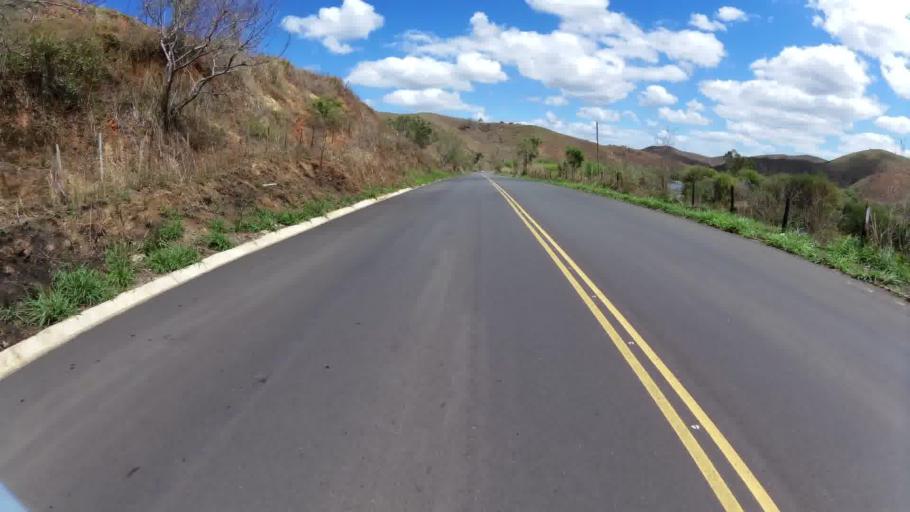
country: BR
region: Rio de Janeiro
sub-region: Itaperuna
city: Itaperuna
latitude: -21.2683
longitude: -41.7753
